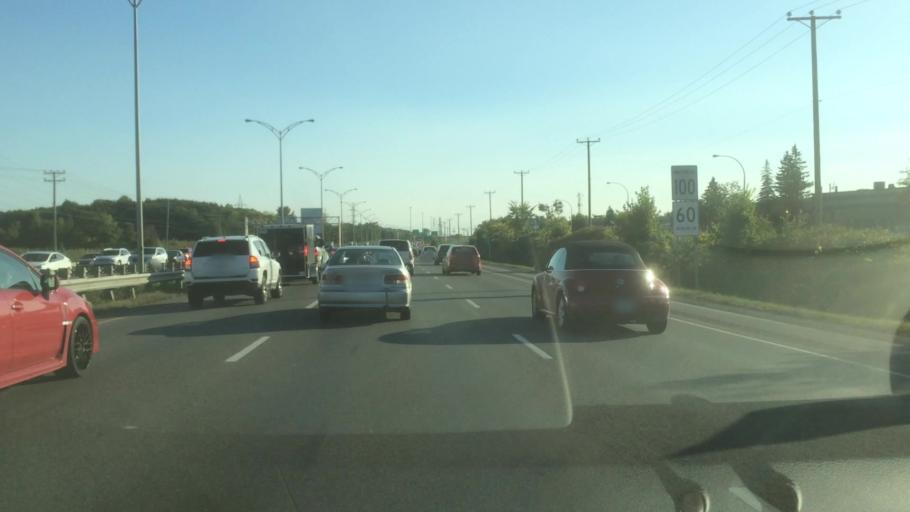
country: CA
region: Quebec
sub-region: Laurentides
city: Boisbriand
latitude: 45.6107
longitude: -73.8544
